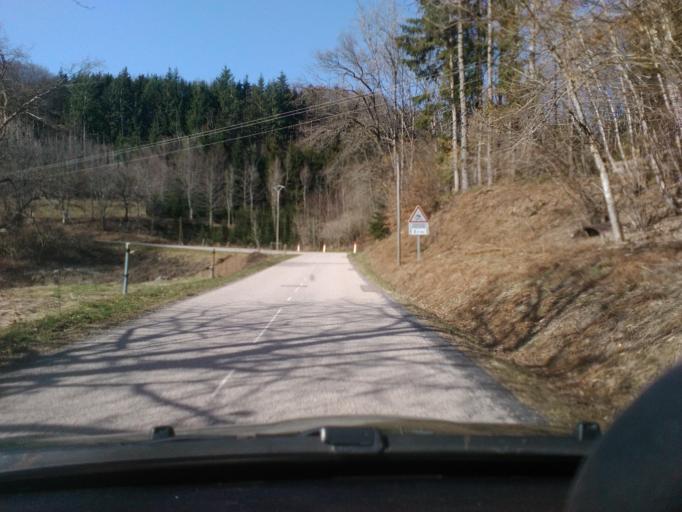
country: FR
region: Lorraine
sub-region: Departement des Vosges
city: Ban-de-Laveline
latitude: 48.3406
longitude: 7.0667
